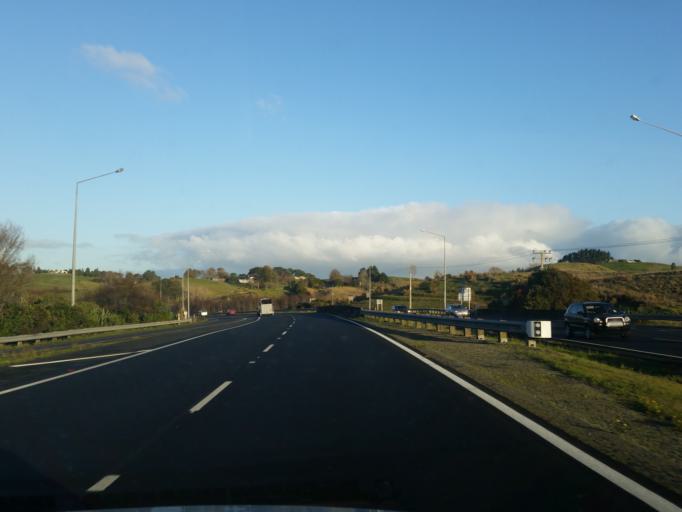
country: NZ
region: Auckland
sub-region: Auckland
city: Pukekohe East
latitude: -37.2499
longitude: 175.0289
